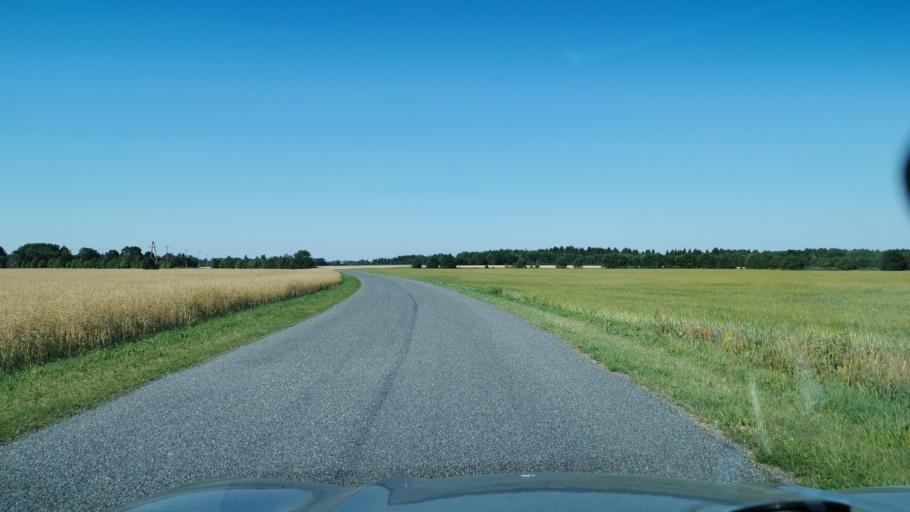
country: EE
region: Harju
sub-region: Paldiski linn
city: Paldiski
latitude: 59.2156
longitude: 24.0423
